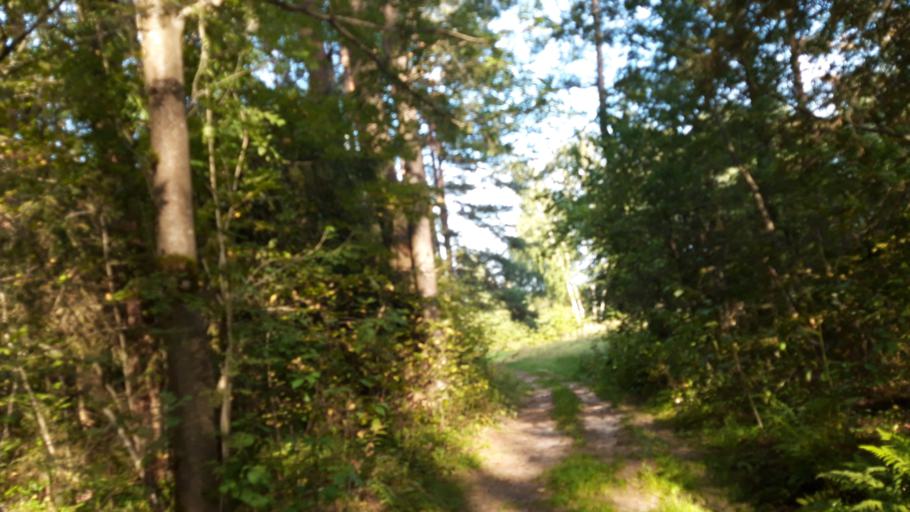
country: RU
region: Tverskaya
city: Konakovo
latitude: 56.6901
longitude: 36.7213
